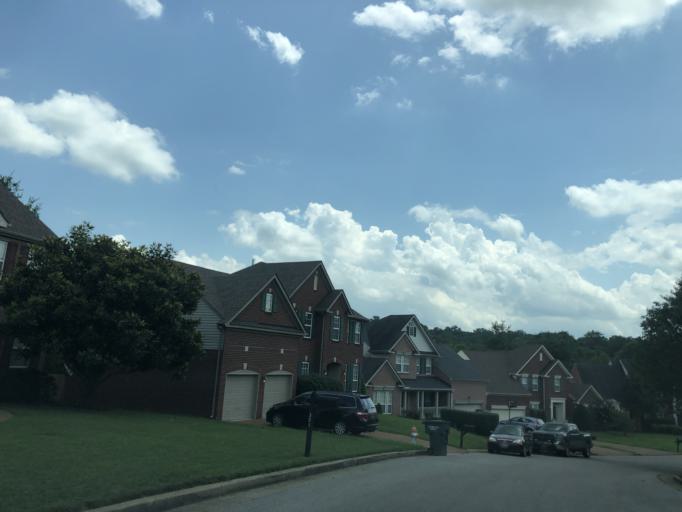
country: US
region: Tennessee
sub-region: Williamson County
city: Brentwood Estates
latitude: 36.0108
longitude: -86.7229
